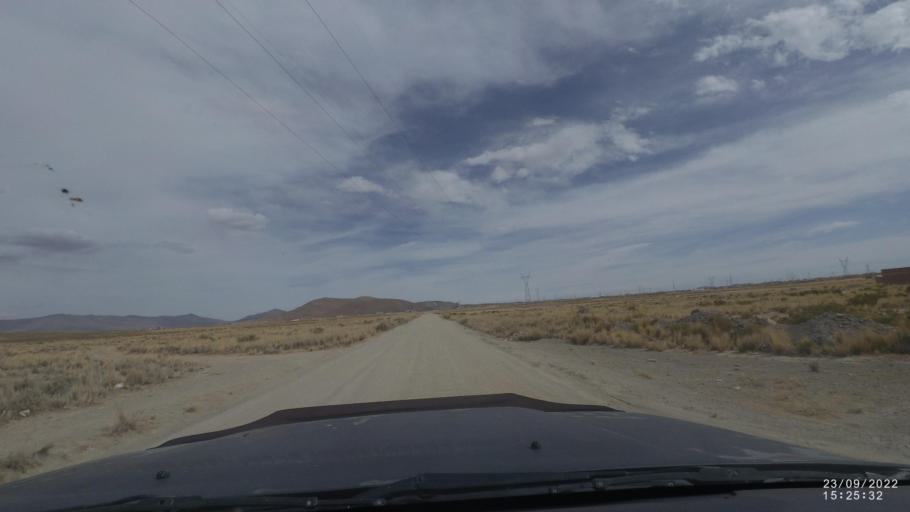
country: BO
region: Oruro
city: Oruro
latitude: -17.9459
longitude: -67.0396
